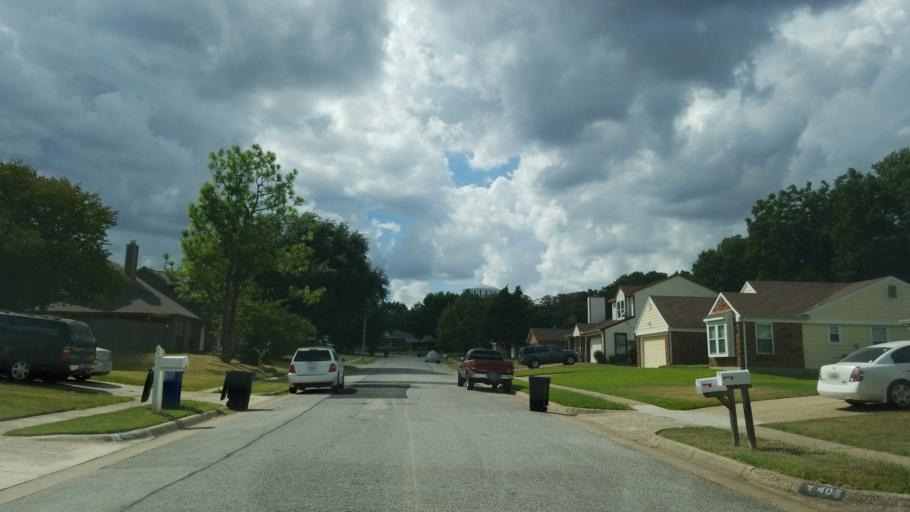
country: US
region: Texas
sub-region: Tarrant County
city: Euless
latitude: 32.8771
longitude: -97.0765
